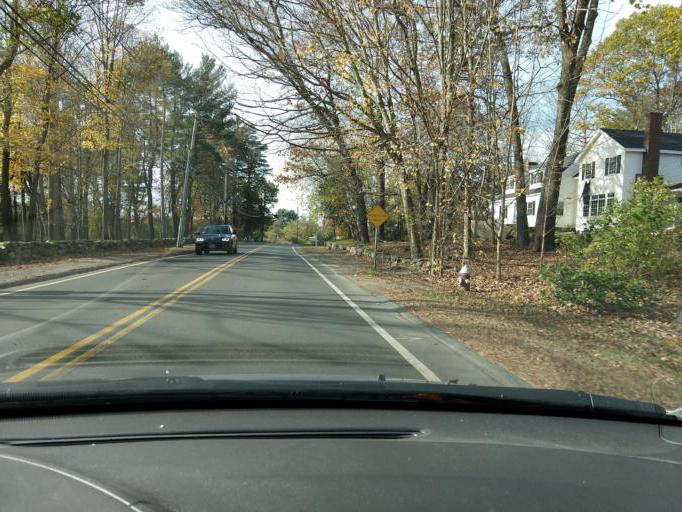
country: US
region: Massachusetts
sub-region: Middlesex County
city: West Concord
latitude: 42.4734
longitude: -71.3771
